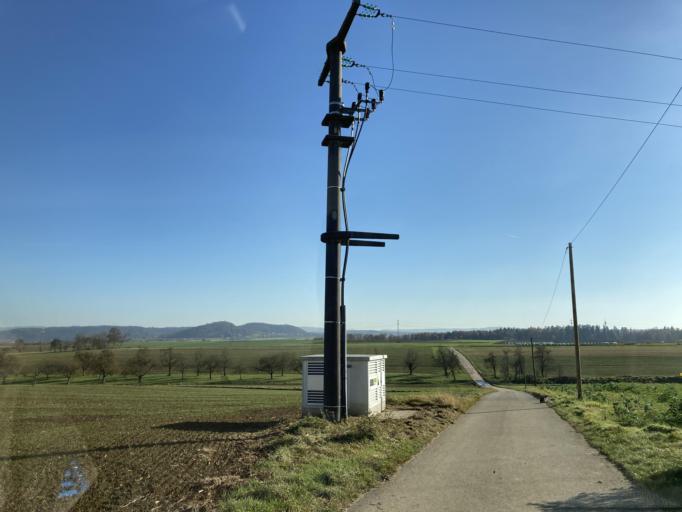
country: DE
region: Baden-Wuerttemberg
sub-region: Tuebingen Region
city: Rottenburg
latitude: 48.4748
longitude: 8.8895
